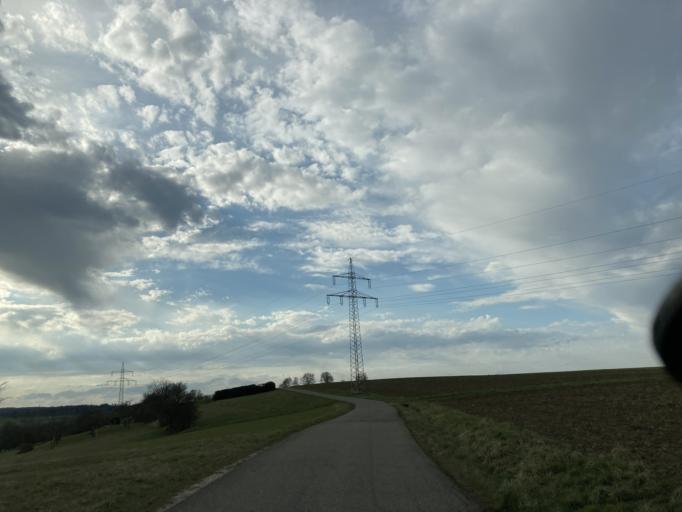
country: DE
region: Baden-Wuerttemberg
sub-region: Tuebingen Region
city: Nehren
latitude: 48.4377
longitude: 9.0743
